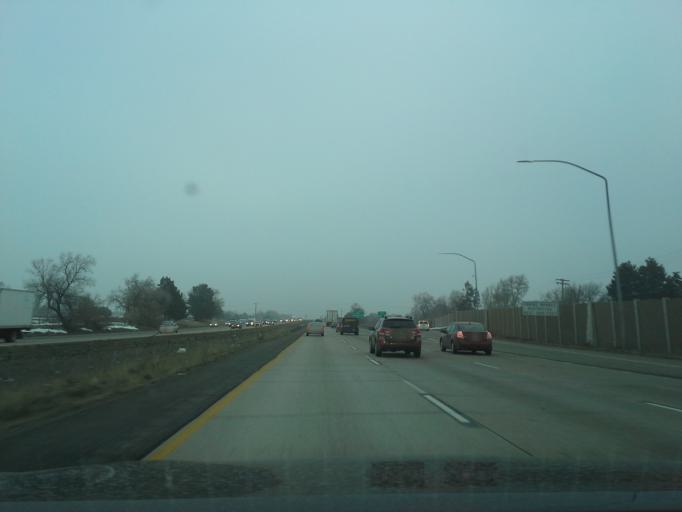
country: US
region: Utah
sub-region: Davis County
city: Clearfield
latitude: 41.1075
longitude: -112.0078
